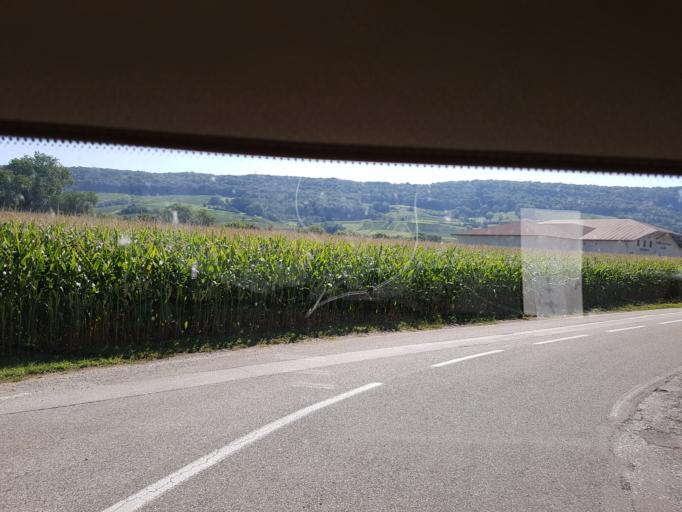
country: FR
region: Franche-Comte
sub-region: Departement du Jura
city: Perrigny
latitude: 46.7270
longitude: 5.5902
